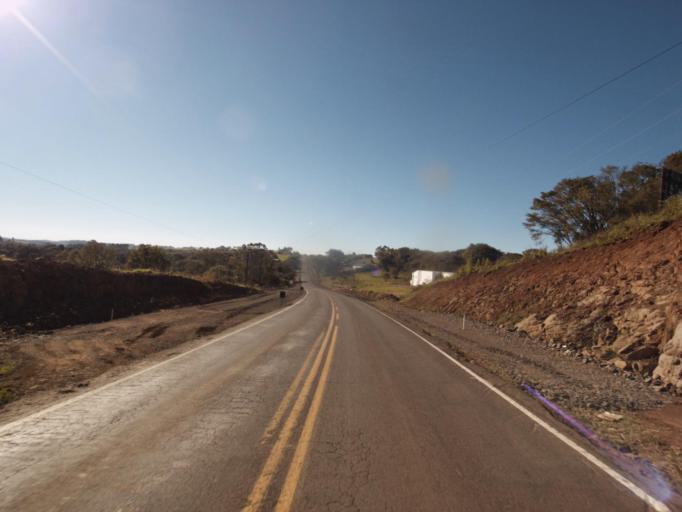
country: AR
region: Misiones
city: Bernardo de Irigoyen
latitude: -26.6897
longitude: -53.5142
